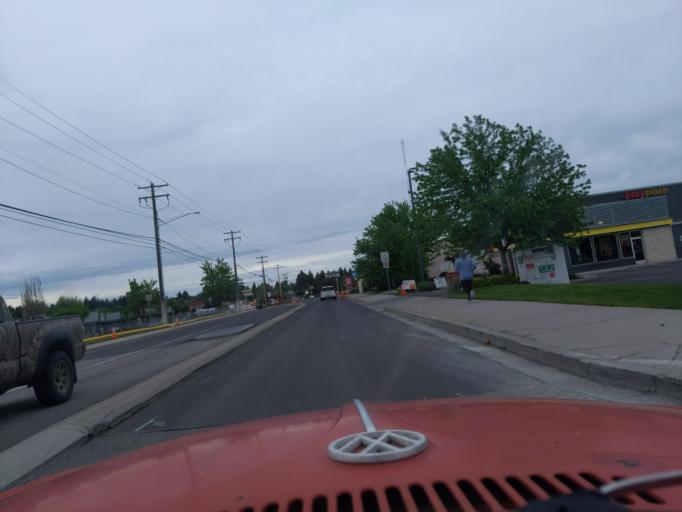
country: US
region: Washington
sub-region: Spokane County
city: Spokane
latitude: 47.6104
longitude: -117.3681
